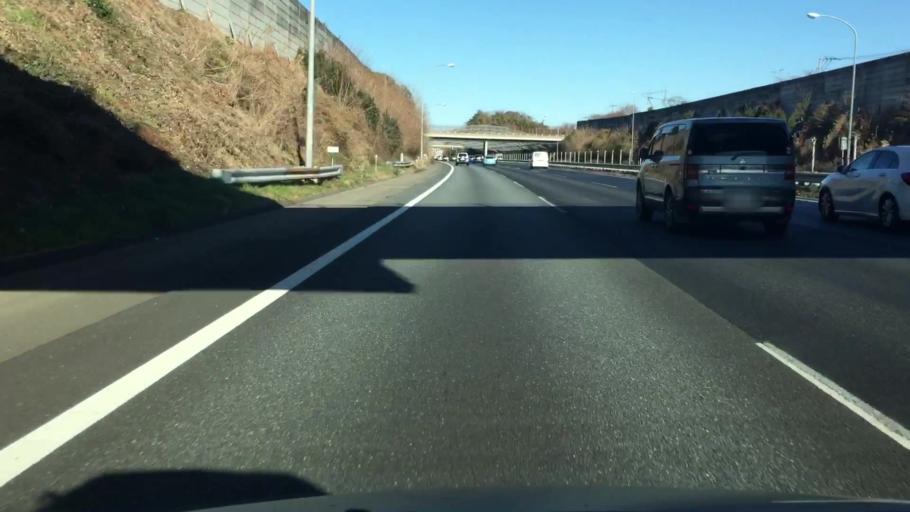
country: JP
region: Saitama
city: Sakado
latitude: 36.0063
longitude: 139.3873
